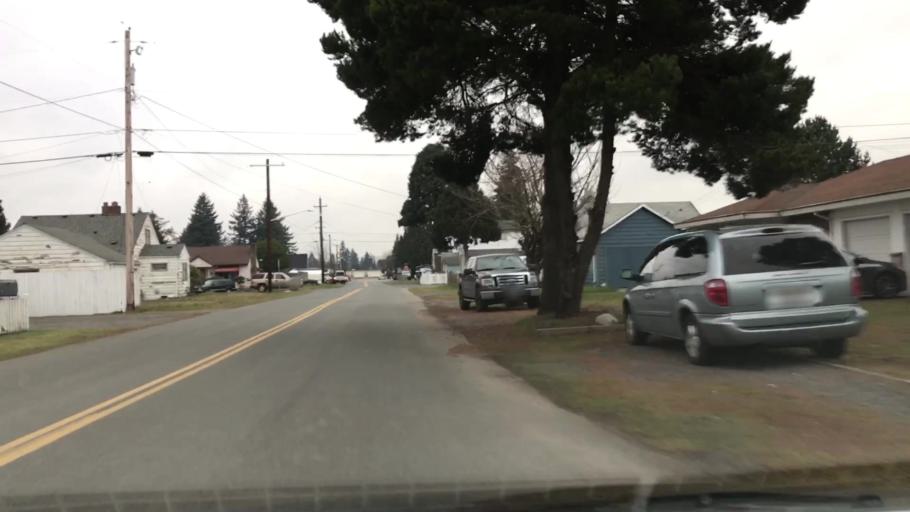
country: US
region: Washington
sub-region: Snohomish County
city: Marysville
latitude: 48.0537
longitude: -122.1696
